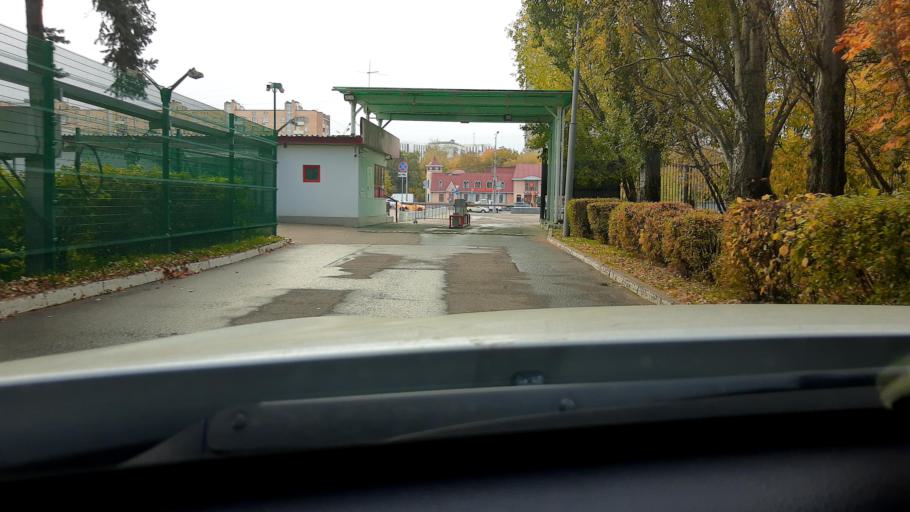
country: RU
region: Moskovskaya
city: Bogorodskoye
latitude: 55.8015
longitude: 37.7402
